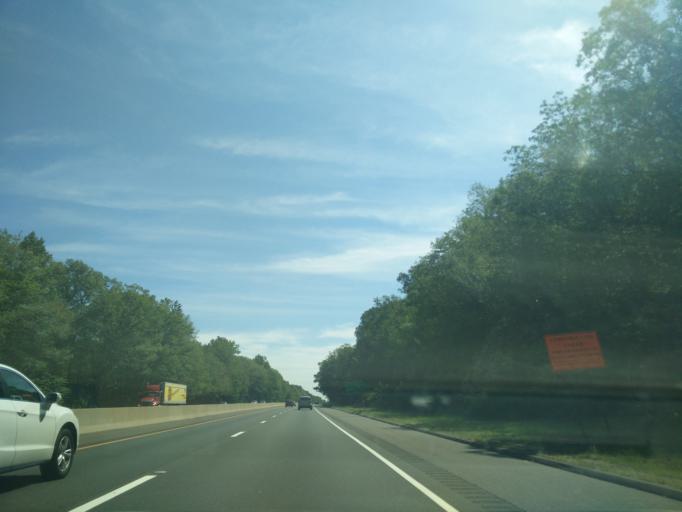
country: US
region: Connecticut
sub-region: New Haven County
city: Guilford
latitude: 41.2974
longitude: -72.7183
